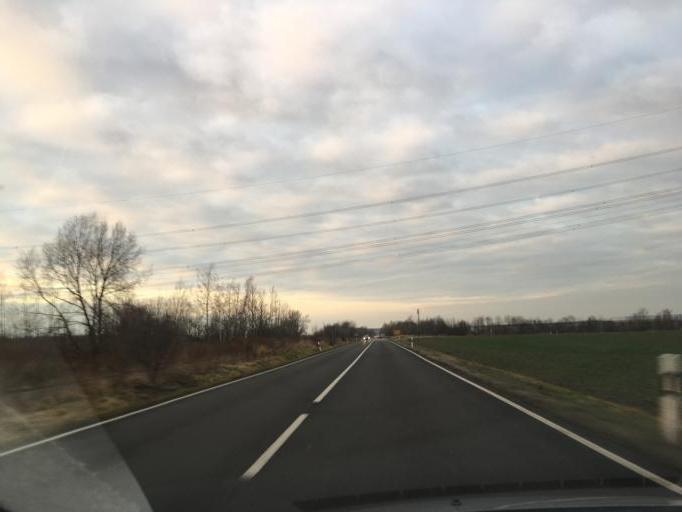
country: DE
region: Saxony
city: Espenhain
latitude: 51.1984
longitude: 12.4590
